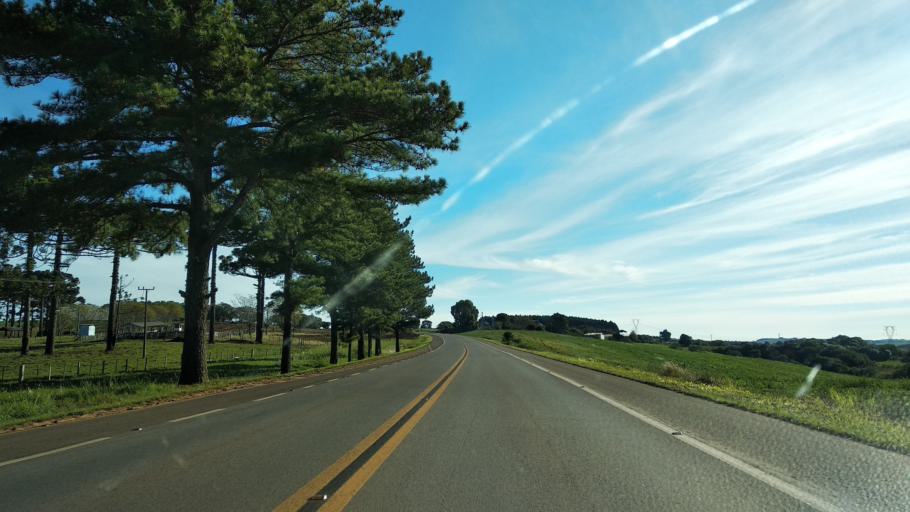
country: BR
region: Santa Catarina
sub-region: Celso Ramos
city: Celso Ramos
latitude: -27.5269
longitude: -51.3751
